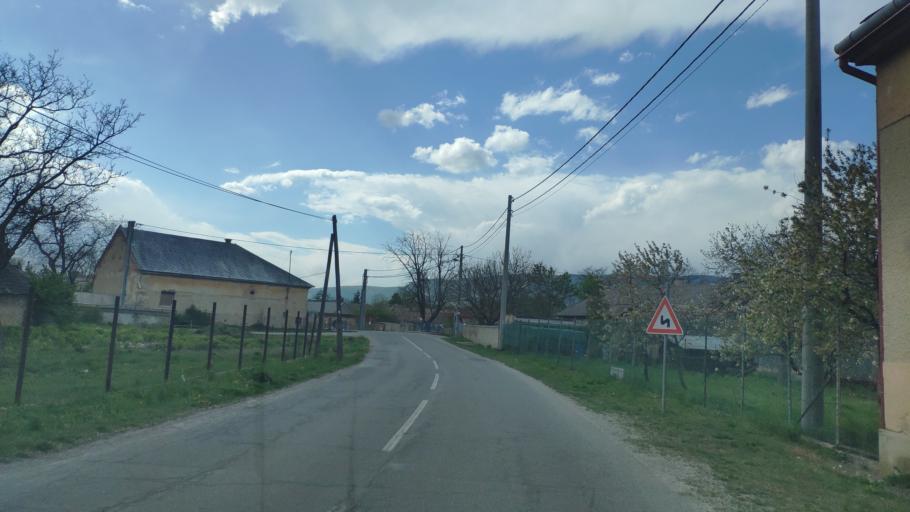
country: SK
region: Kosicky
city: Medzev
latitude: 48.5976
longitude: 20.8792
